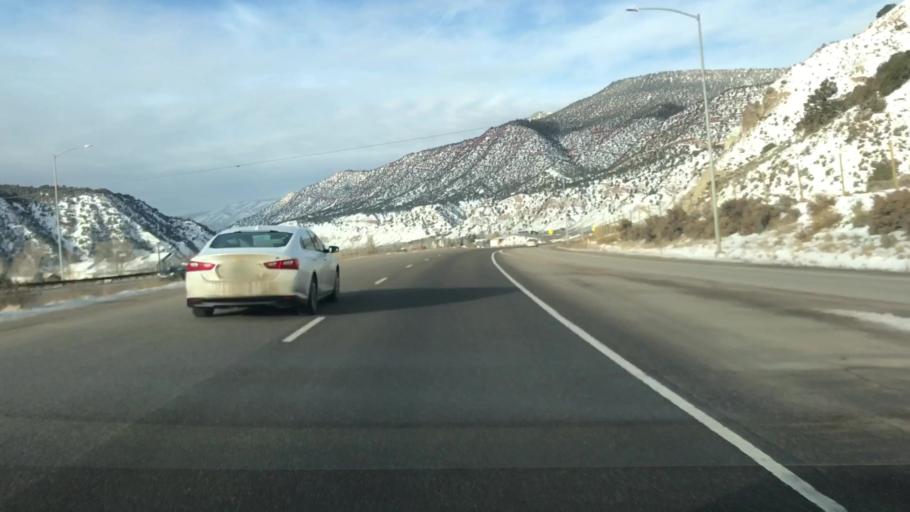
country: US
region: Colorado
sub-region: Eagle County
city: Gypsum
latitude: 39.6523
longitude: -106.9592
